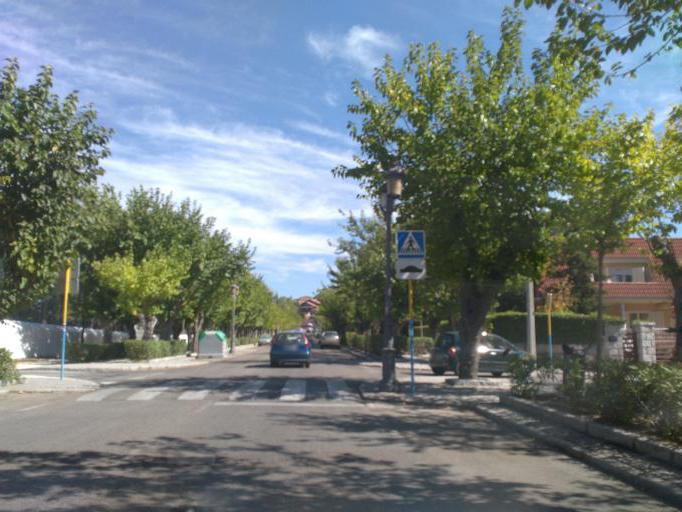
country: ES
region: Madrid
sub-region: Provincia de Madrid
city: Torrelodones
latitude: 40.5820
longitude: -3.9544
